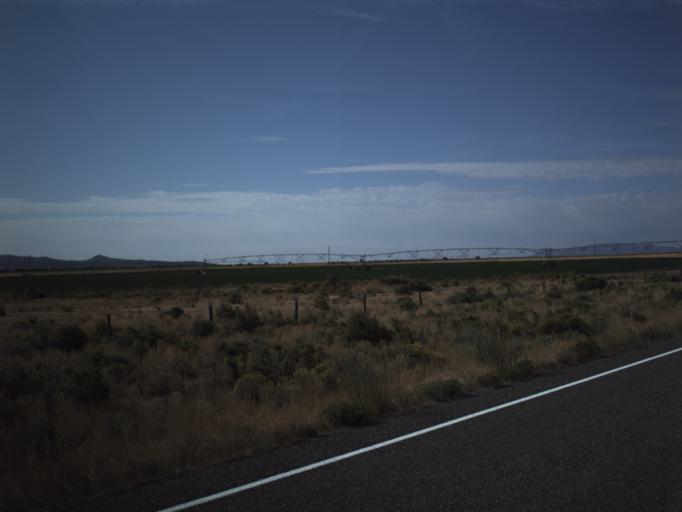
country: US
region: Idaho
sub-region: Cassia County
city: Burley
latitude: 41.7668
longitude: -113.5070
